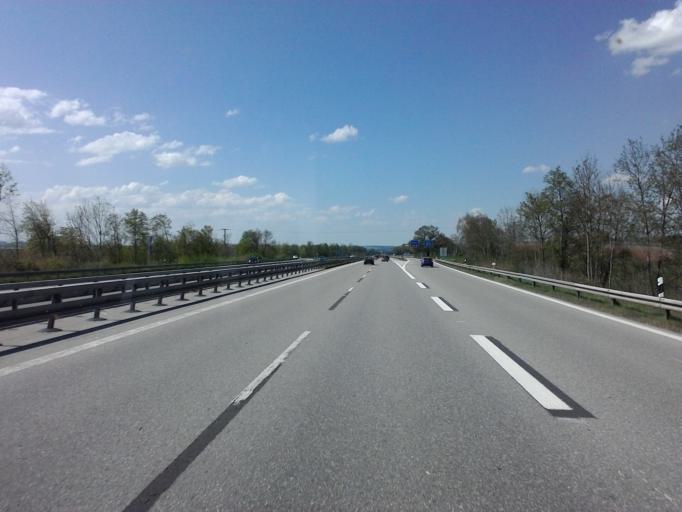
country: DE
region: Bavaria
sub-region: Swabia
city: Kempten (Allgaeu)
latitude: 47.7357
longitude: 10.3455
